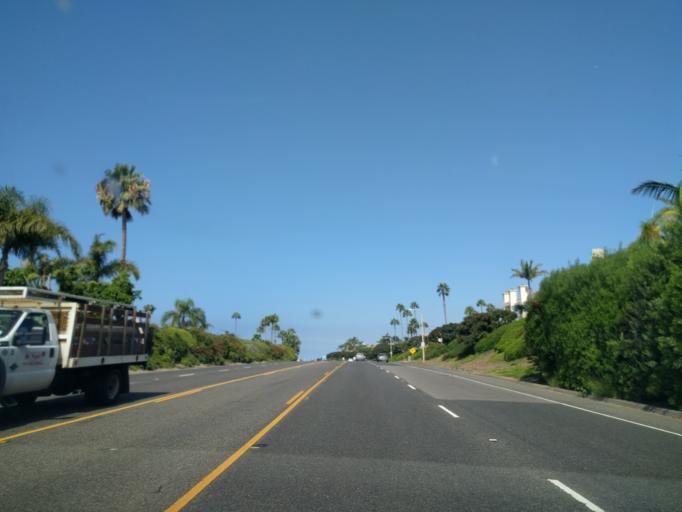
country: US
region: California
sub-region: Orange County
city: Laguna Beach
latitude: 33.5547
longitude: -117.8123
